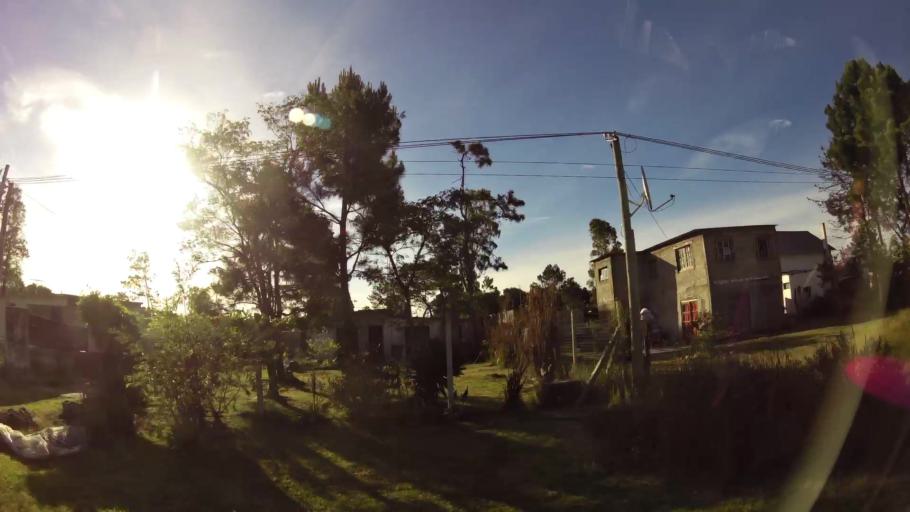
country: UY
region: Canelones
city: Empalme Olmos
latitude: -34.7687
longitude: -55.8573
